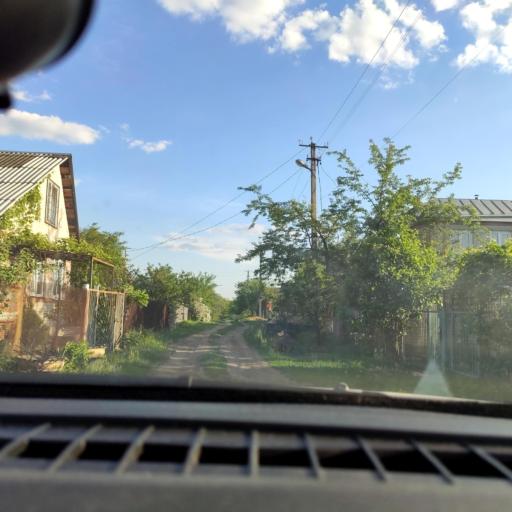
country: RU
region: Voronezj
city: Maslovka
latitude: 51.5192
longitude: 39.2381
